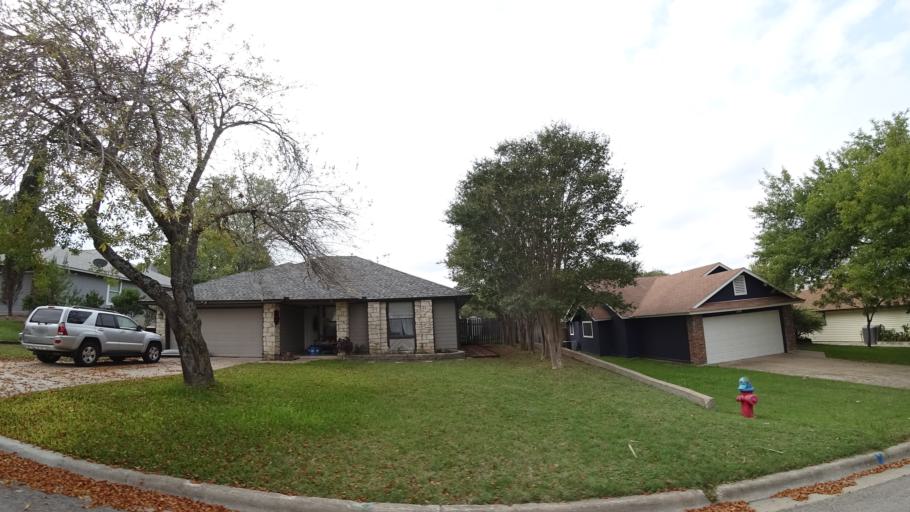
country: US
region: Texas
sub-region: Williamson County
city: Round Rock
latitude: 30.4875
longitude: -97.6868
